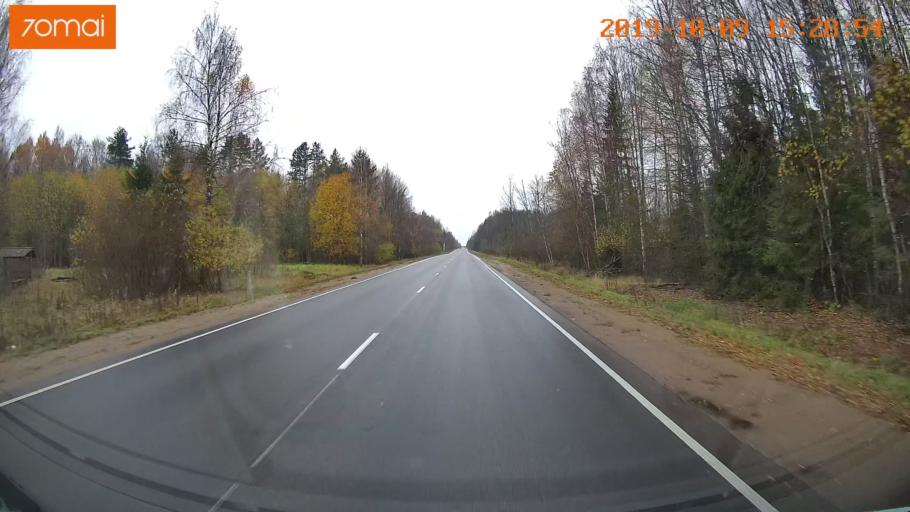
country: RU
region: Kostroma
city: Susanino
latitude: 57.9976
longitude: 41.3519
